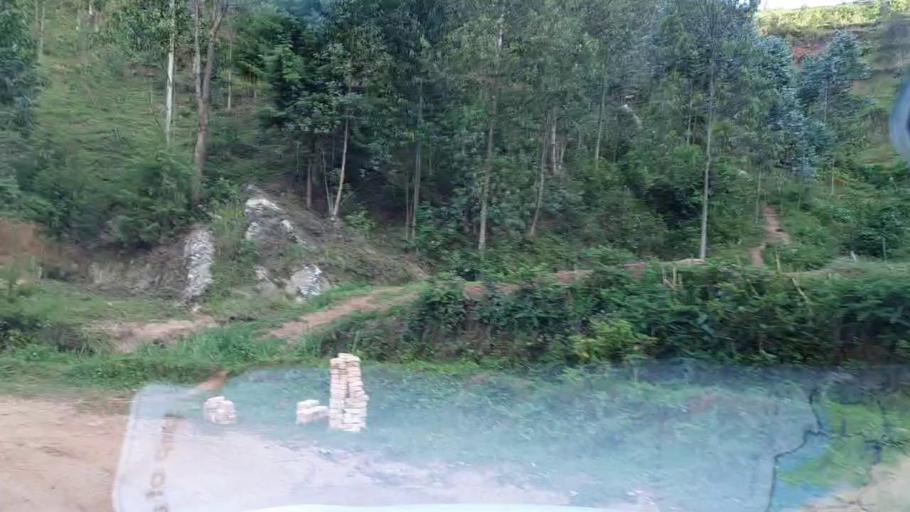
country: RW
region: Southern Province
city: Gikongoro
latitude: -2.4046
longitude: 29.5549
